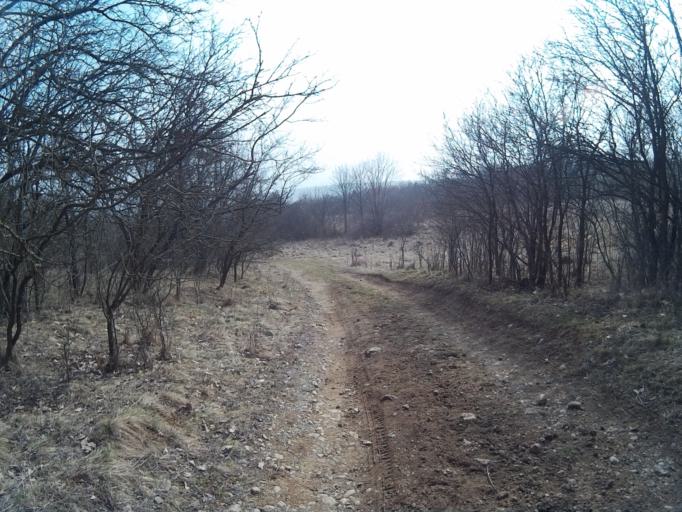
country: CZ
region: South Moravian
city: Pozorice
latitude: 49.2152
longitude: 16.8063
